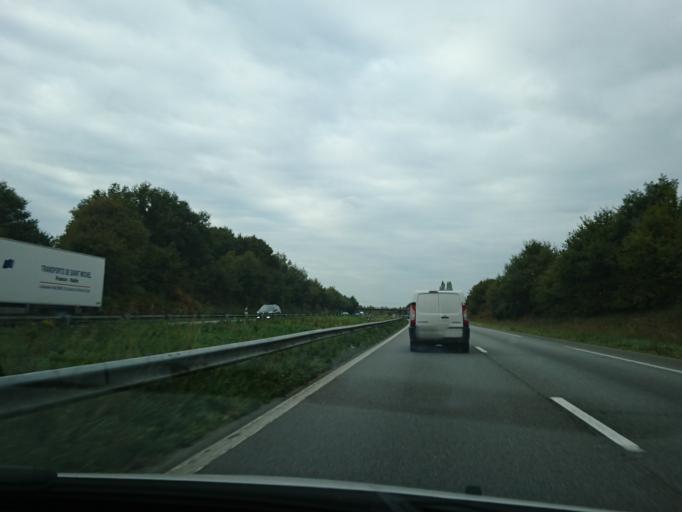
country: FR
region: Pays de la Loire
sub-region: Departement de la Loire-Atlantique
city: Le Temple-de-Bretagne
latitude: 47.3329
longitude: -1.7907
